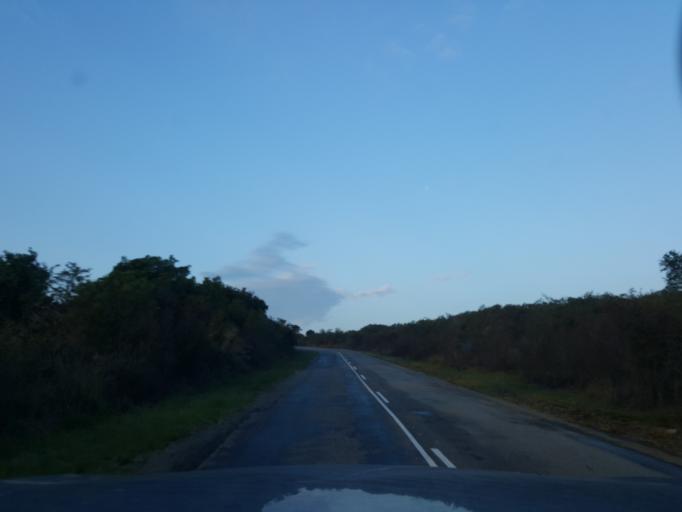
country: ZA
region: Eastern Cape
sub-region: Cacadu District Municipality
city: Grahamstown
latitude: -33.4622
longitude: 26.4925
